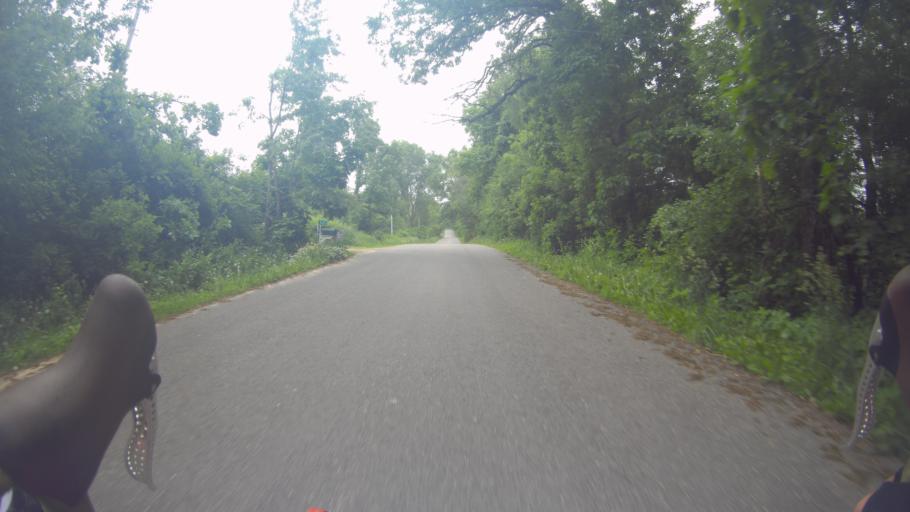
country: US
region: Wisconsin
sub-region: Green County
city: Brooklyn
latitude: 42.8707
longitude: -89.3597
